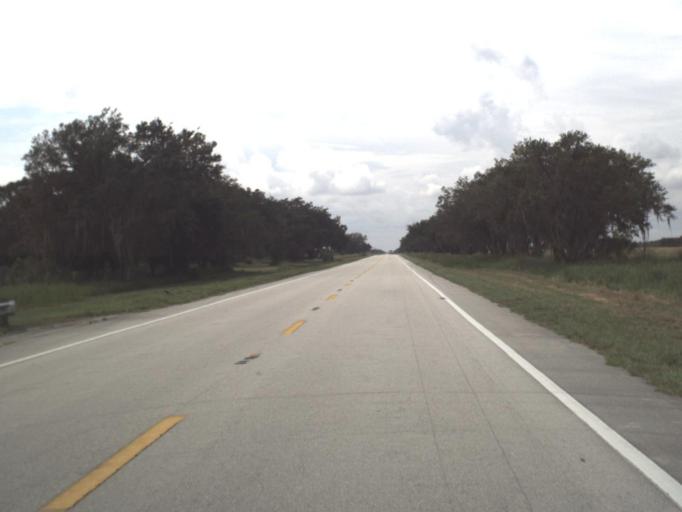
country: US
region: Florida
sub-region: Hendry County
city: Port LaBelle
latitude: 26.8374
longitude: -81.3913
